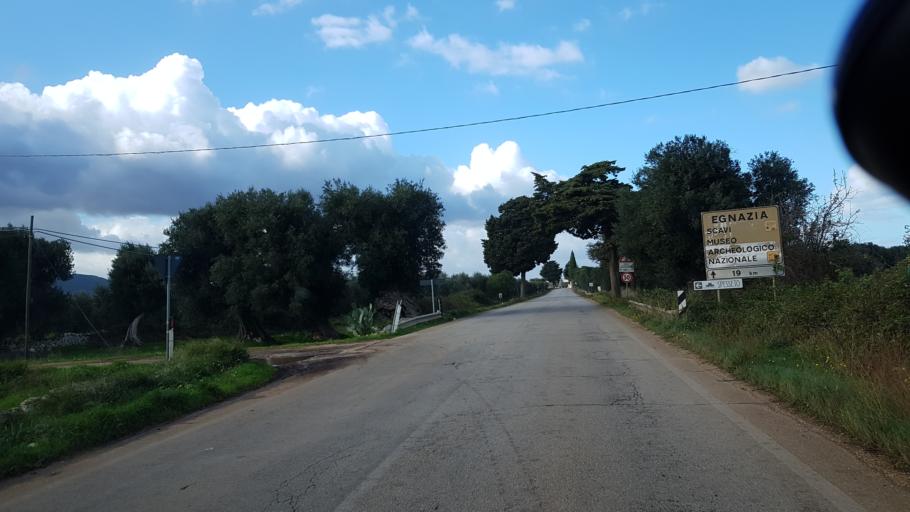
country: IT
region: Apulia
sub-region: Provincia di Brindisi
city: Montalbano
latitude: 40.7877
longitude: 17.4687
